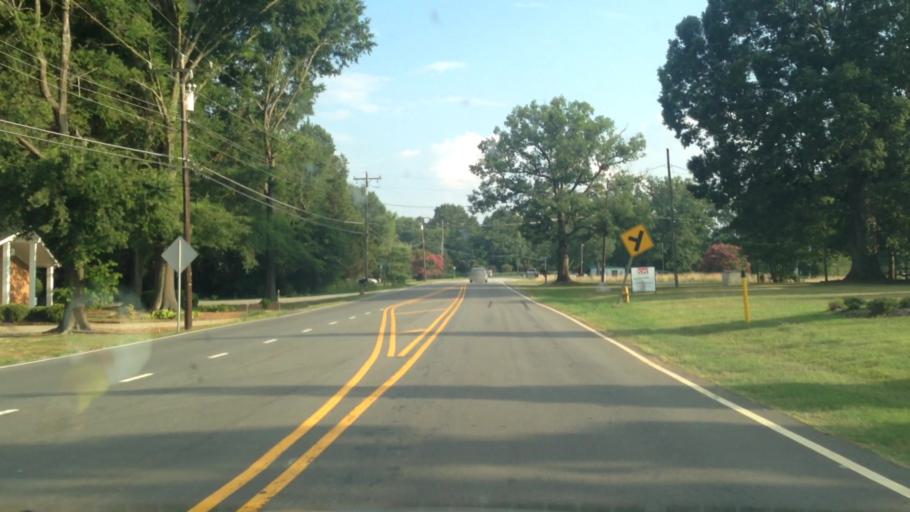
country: US
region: North Carolina
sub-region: Forsyth County
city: Kernersville
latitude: 36.0715
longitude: -80.0590
